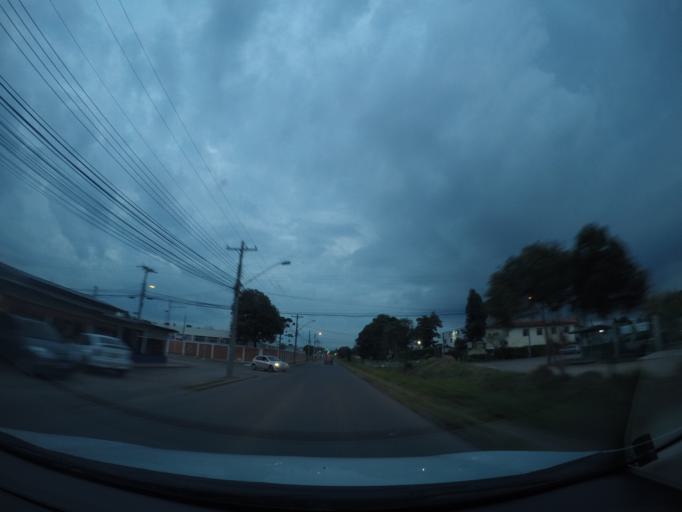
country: BR
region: Parana
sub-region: Sao Jose Dos Pinhais
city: Sao Jose dos Pinhais
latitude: -25.4938
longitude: -49.2355
